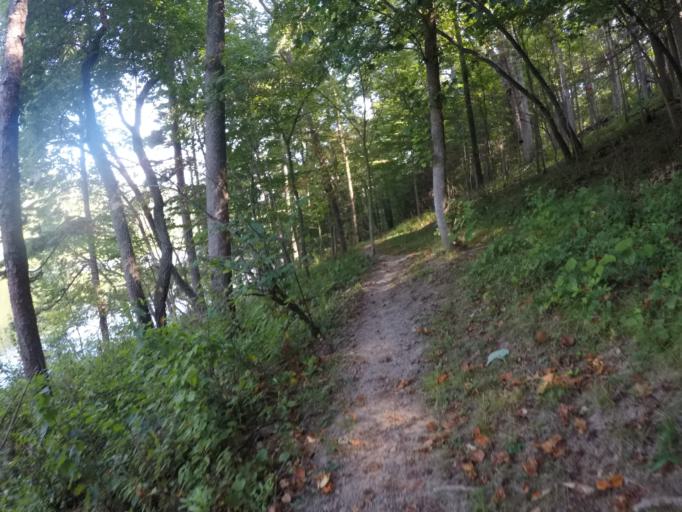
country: US
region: Ohio
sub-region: Lawrence County
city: Ironton
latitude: 38.6143
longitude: -82.6274
